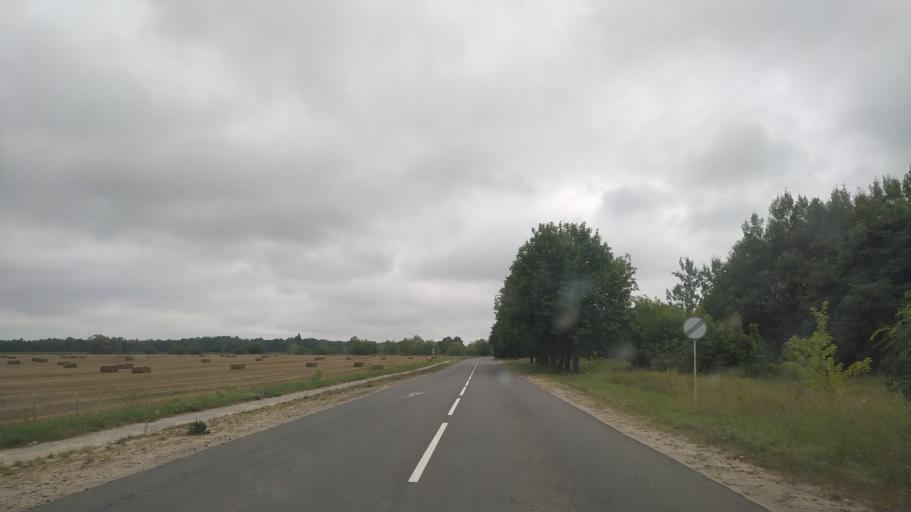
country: BY
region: Brest
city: Byaroza
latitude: 52.5556
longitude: 24.9207
